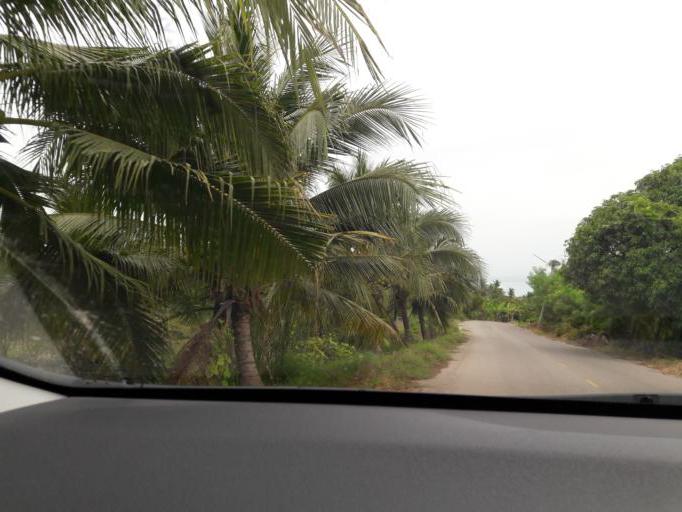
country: TH
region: Ratchaburi
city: Damnoen Saduak
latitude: 13.5671
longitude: 100.0213
